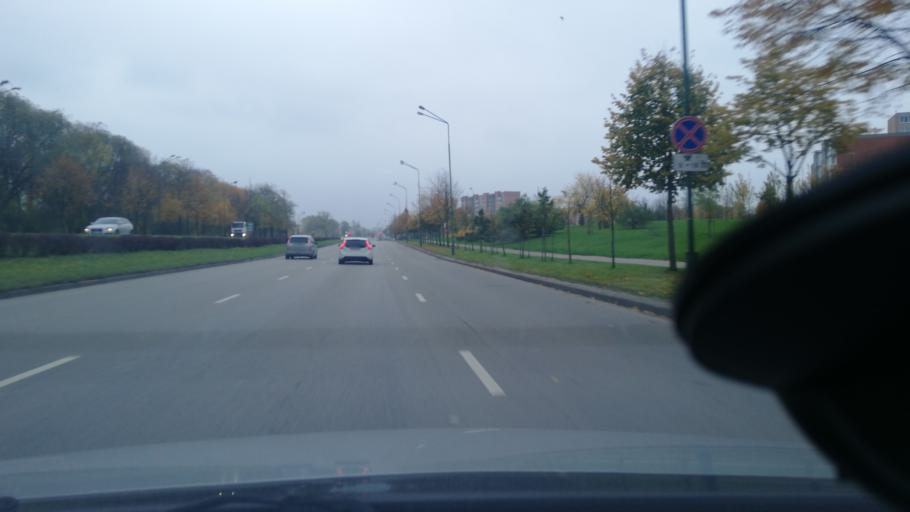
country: LT
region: Klaipedos apskritis
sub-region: Klaipeda
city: Klaipeda
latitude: 55.6741
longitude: 21.1957
